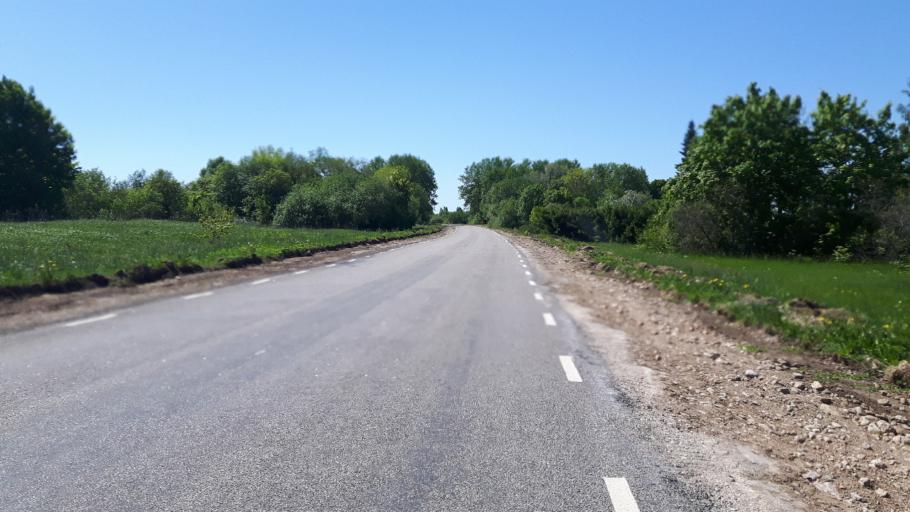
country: EE
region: Ida-Virumaa
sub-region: Narva-Joesuu linn
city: Narva-Joesuu
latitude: 59.3935
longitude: 27.9243
